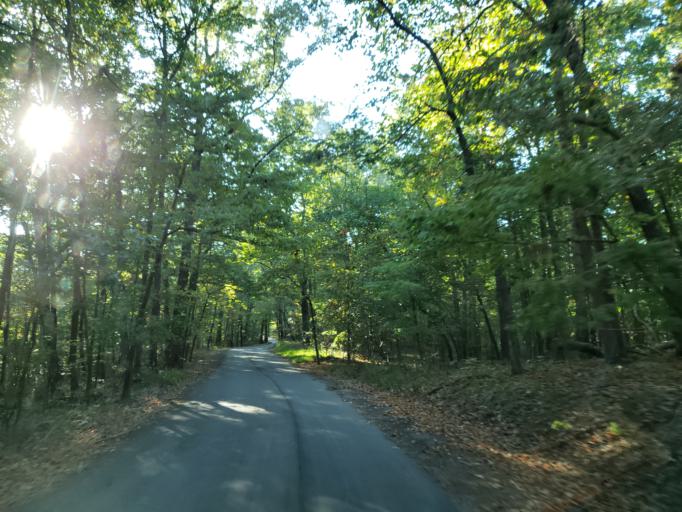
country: US
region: Georgia
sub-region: Pickens County
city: Jasper
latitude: 34.4304
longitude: -84.3979
